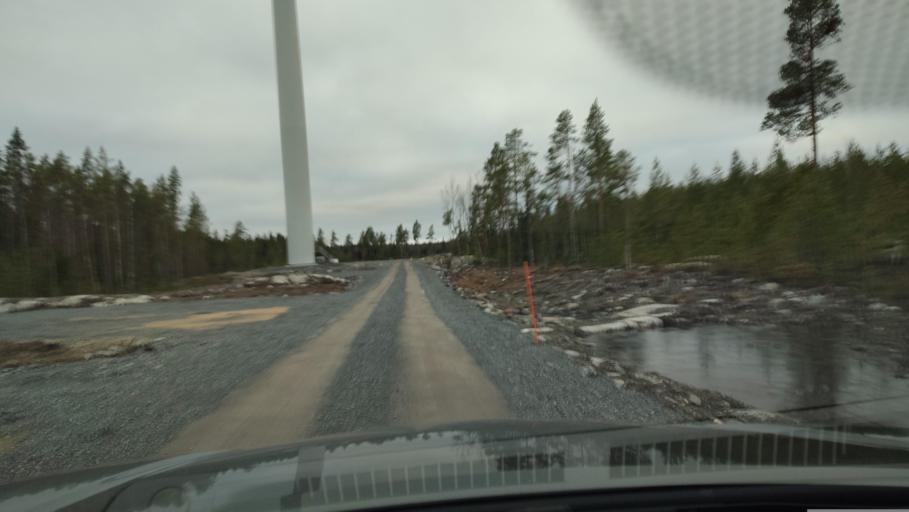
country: FI
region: Ostrobothnia
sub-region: Sydosterbotten
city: Kristinestad
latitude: 62.2004
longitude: 21.5506
